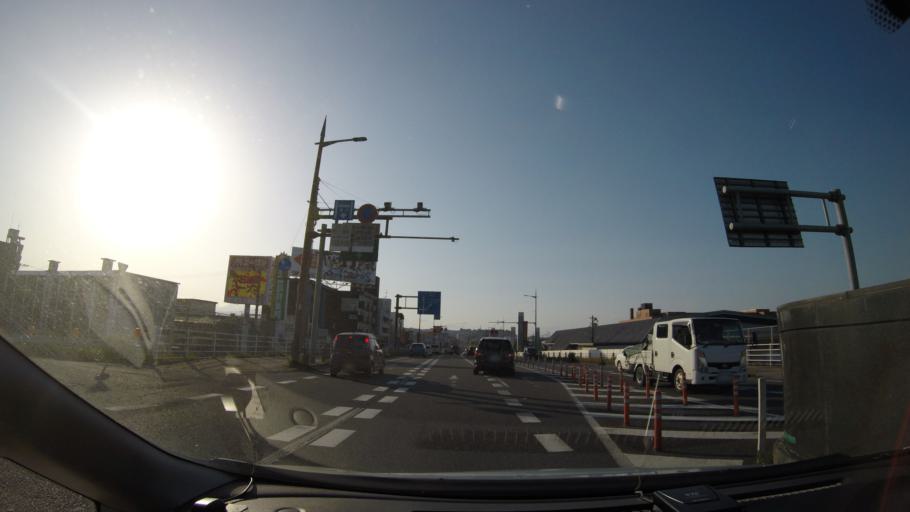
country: JP
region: Oita
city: Oita
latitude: 33.2037
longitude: 131.6044
